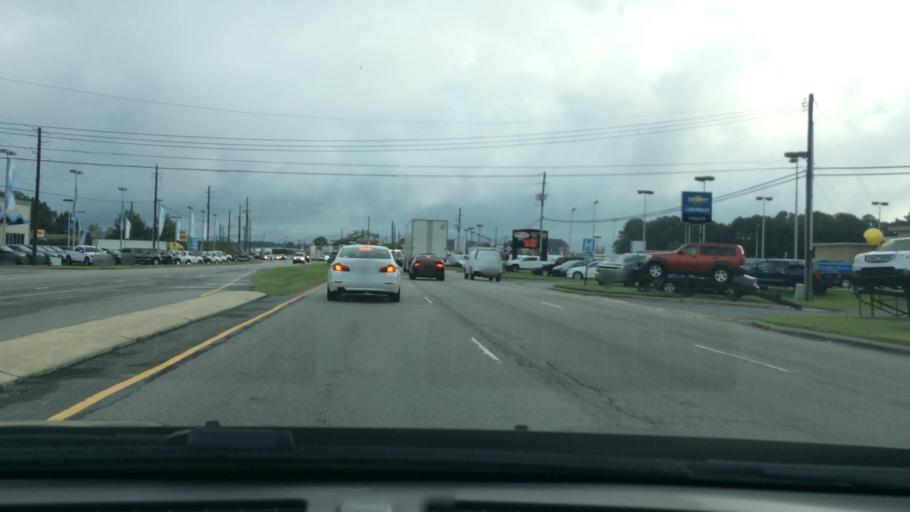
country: US
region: North Carolina
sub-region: Pitt County
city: Summerfield
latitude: 35.5700
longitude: -77.4049
